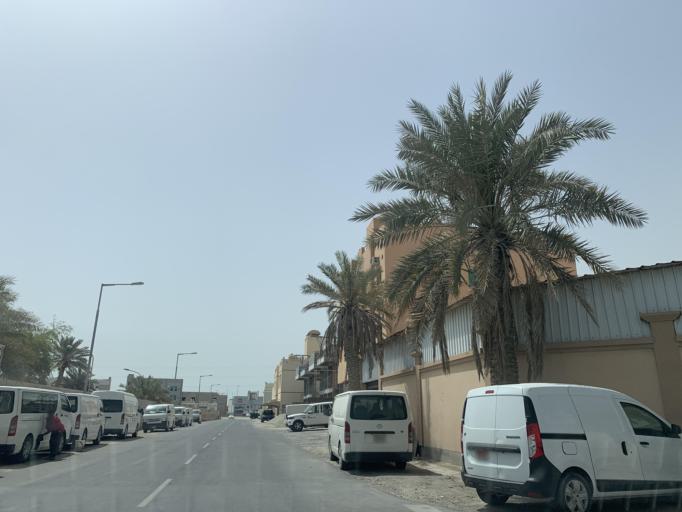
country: BH
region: Northern
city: Sitrah
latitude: 26.1370
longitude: 50.6036
